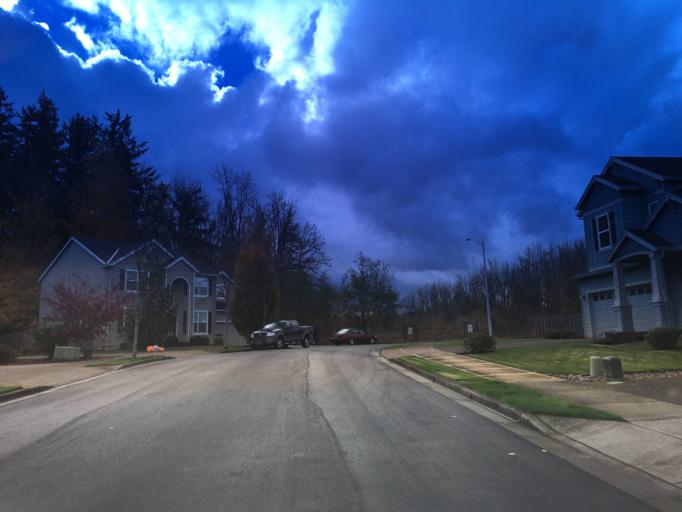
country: US
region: Oregon
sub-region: Multnomah County
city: Troutdale
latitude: 45.5099
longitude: -122.3822
